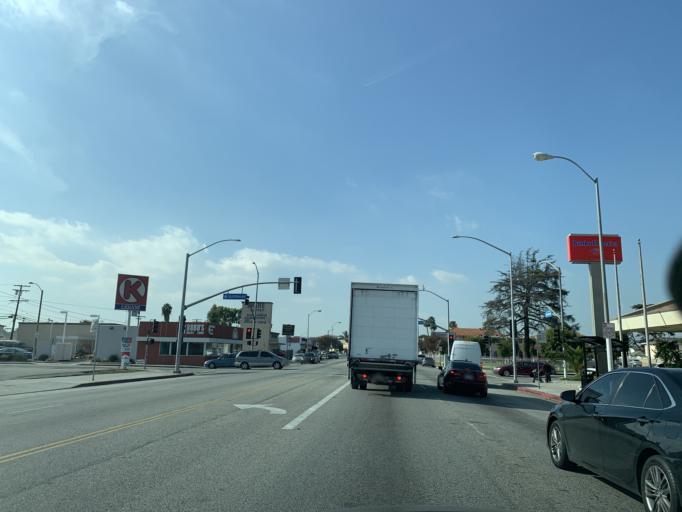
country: US
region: California
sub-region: Los Angeles County
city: Lynwood
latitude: 33.9307
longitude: -118.2081
